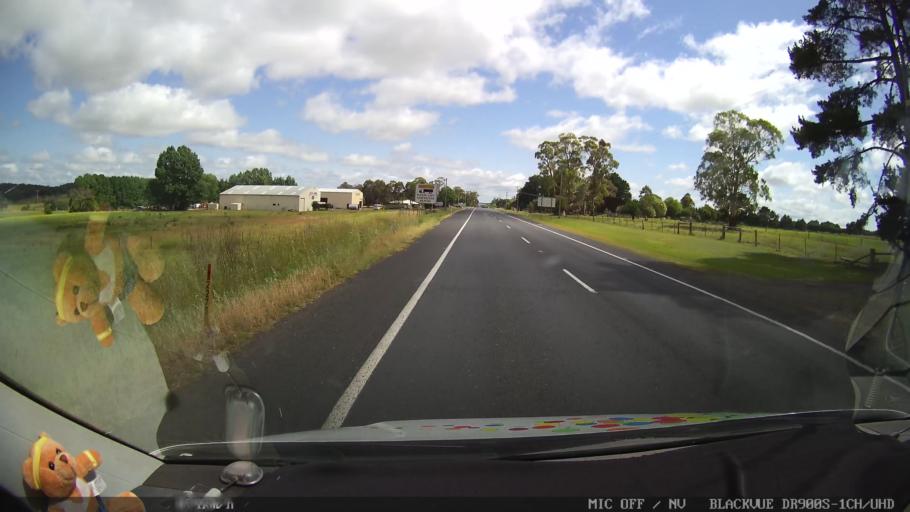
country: AU
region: New South Wales
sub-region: Glen Innes Severn
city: Glen Innes
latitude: -29.7673
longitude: 151.7326
